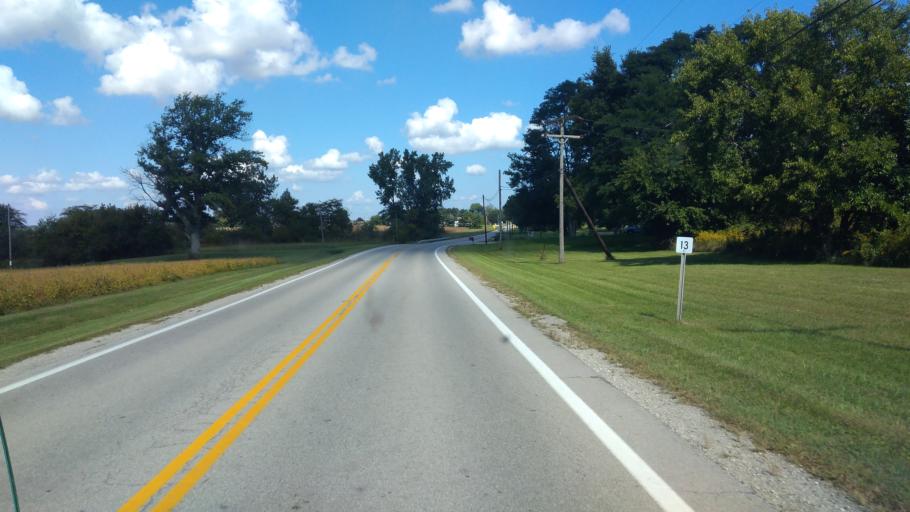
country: US
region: Ohio
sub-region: Marion County
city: Marion
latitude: 40.6395
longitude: -83.1448
